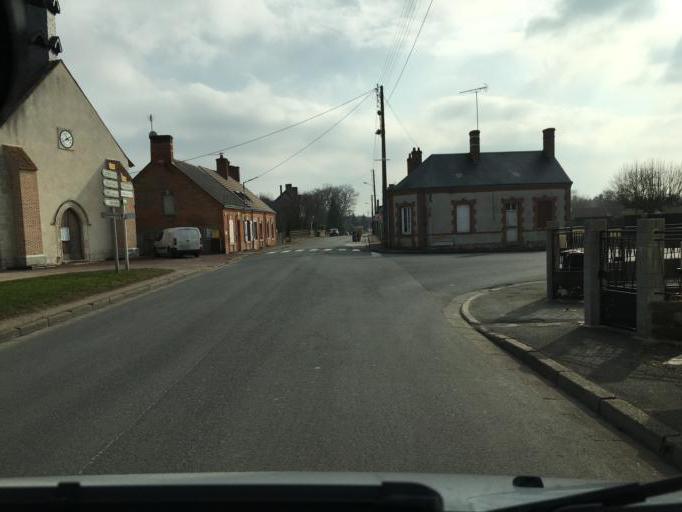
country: FR
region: Centre
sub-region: Departement du Loir-et-Cher
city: Neung-sur-Beuvron
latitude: 47.5845
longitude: 1.7793
